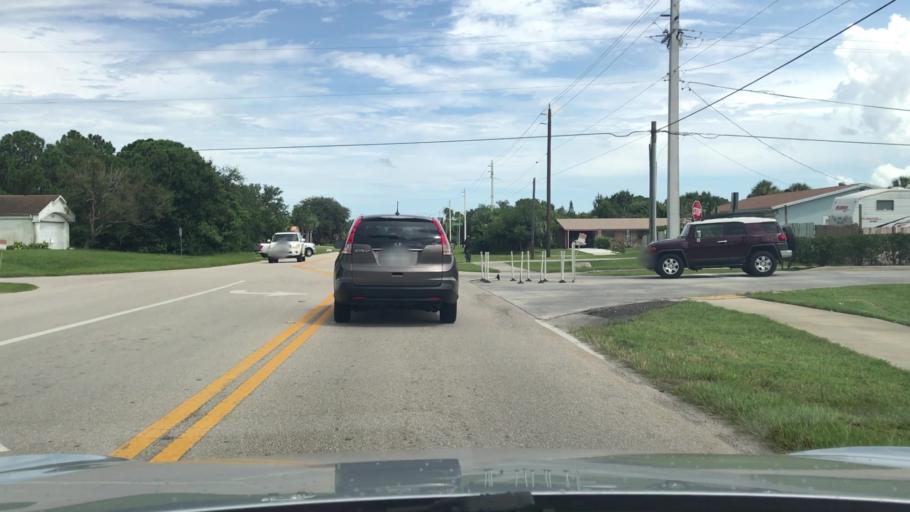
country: US
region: Florida
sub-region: Indian River County
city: Sebastian
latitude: 27.7838
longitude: -80.4926
